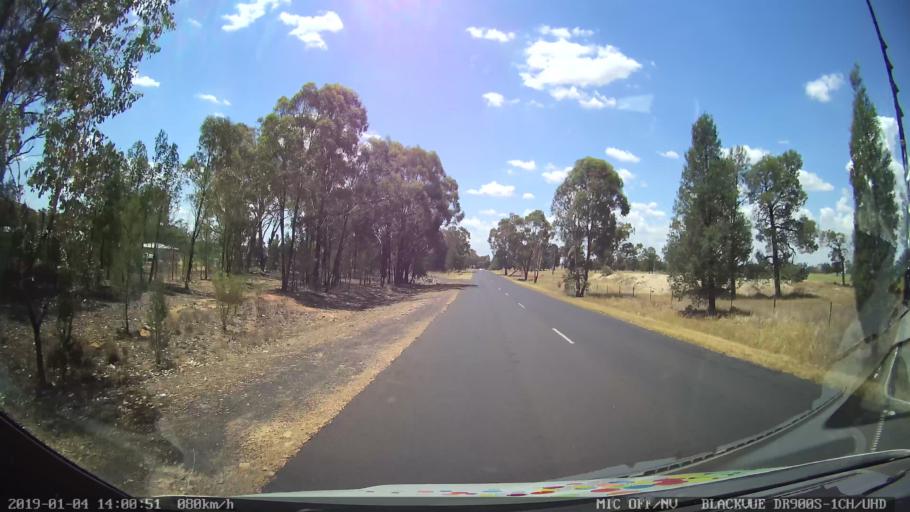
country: AU
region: New South Wales
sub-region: Dubbo Municipality
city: Dubbo
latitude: -32.3027
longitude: 148.5961
